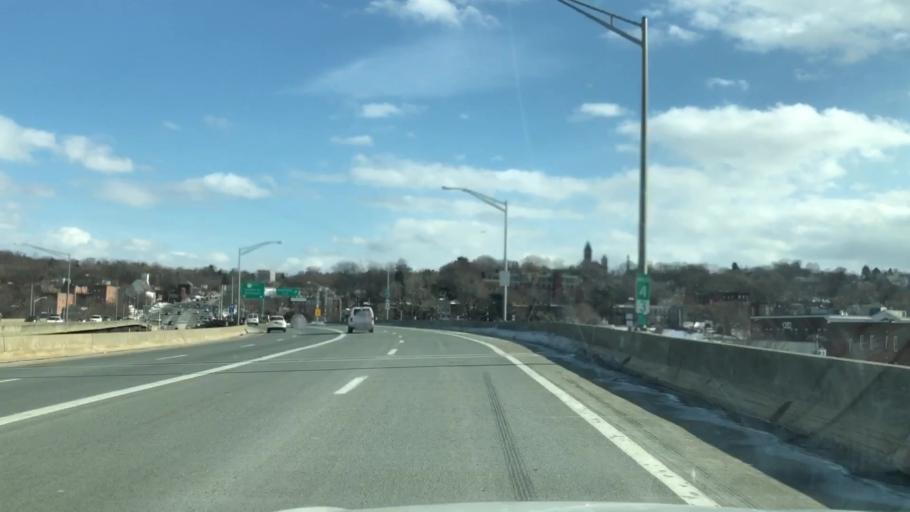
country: US
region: New York
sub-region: Albany County
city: Green Island
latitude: 42.7391
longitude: -73.6874
